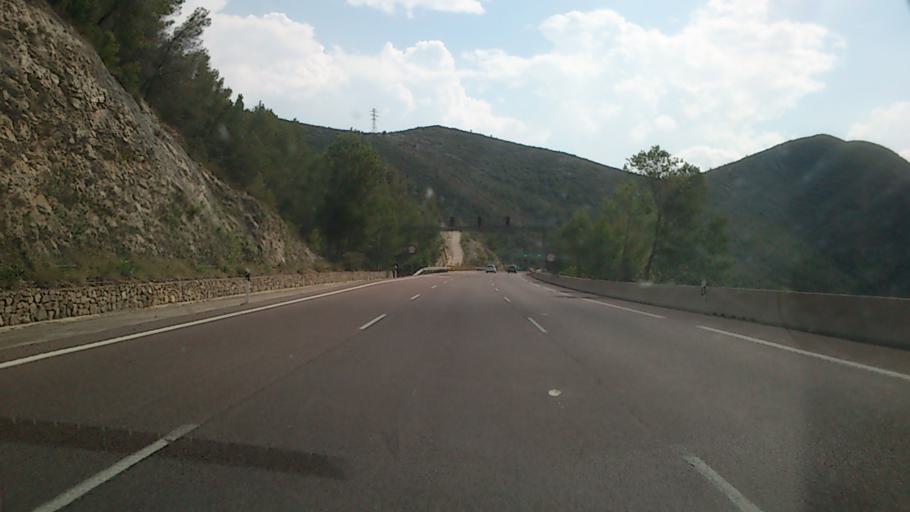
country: ES
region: Valencia
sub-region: Provincia de Valencia
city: L'Olleria
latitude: 38.9319
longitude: -0.5739
